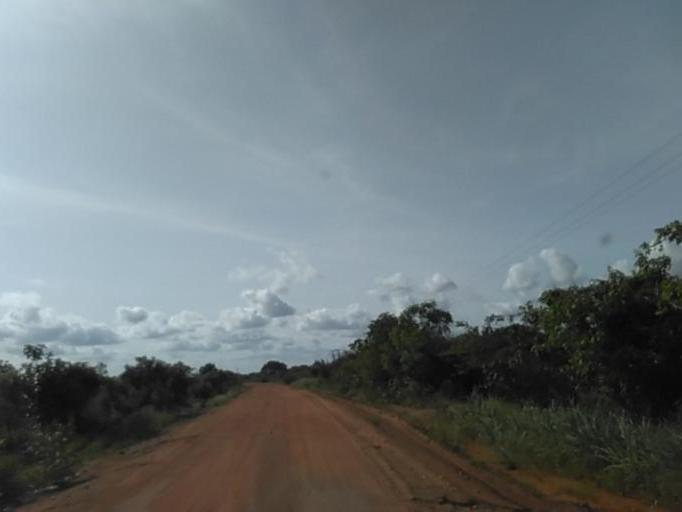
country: GH
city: Akropong
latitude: 6.0732
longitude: 0.2834
